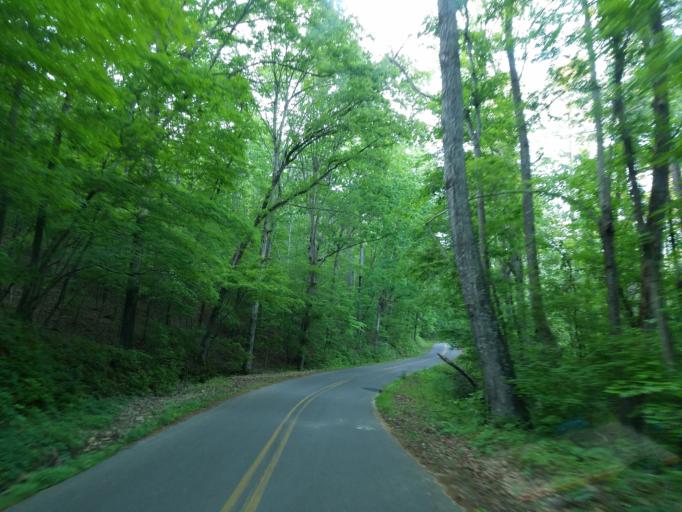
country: US
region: Georgia
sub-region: Gordon County
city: Calhoun
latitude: 34.5610
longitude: -85.1028
